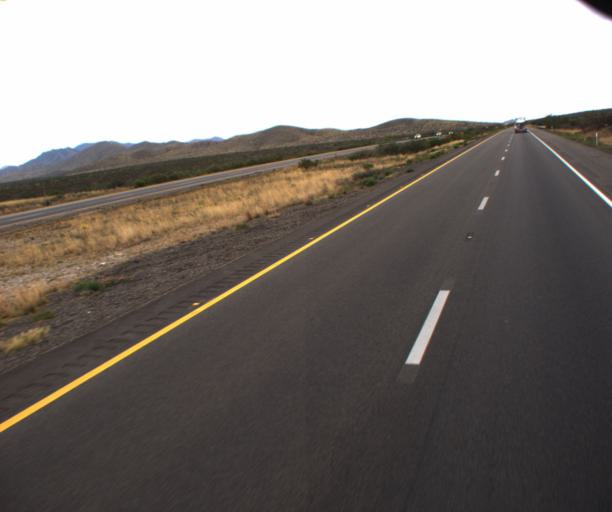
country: US
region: Arizona
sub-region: Cochise County
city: Willcox
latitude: 32.1297
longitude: -110.0098
